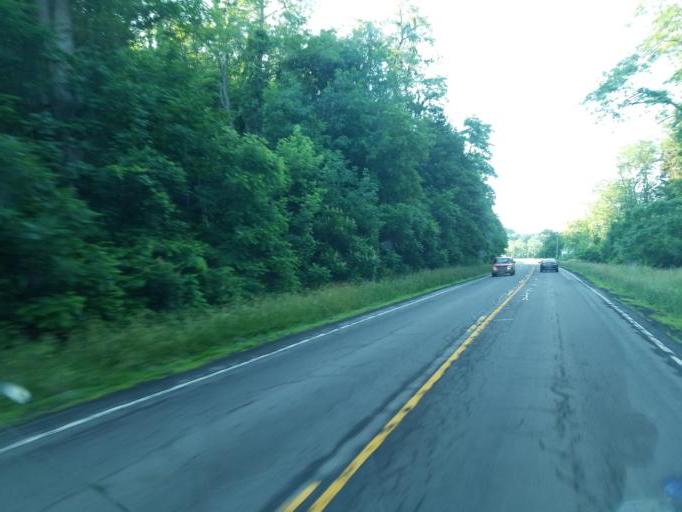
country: US
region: New York
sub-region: Wayne County
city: Clyde
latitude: 43.0476
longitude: -76.8651
